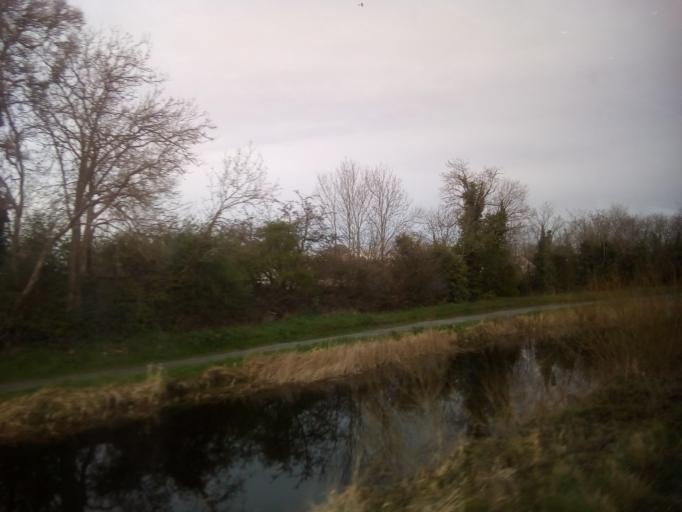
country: IE
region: Leinster
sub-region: Kildare
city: Maynooth
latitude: 53.3800
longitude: -6.5775
